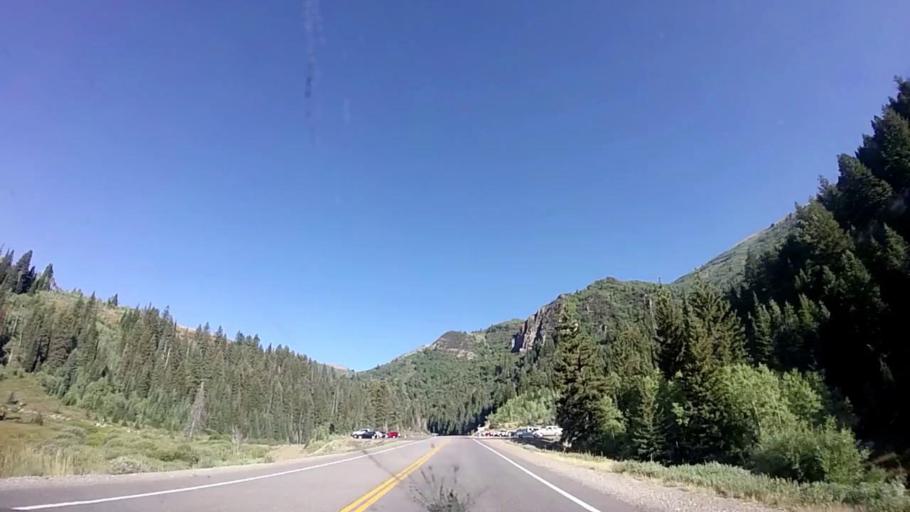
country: US
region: Utah
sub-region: Summit County
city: Summit Park
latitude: 40.6486
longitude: -111.6467
